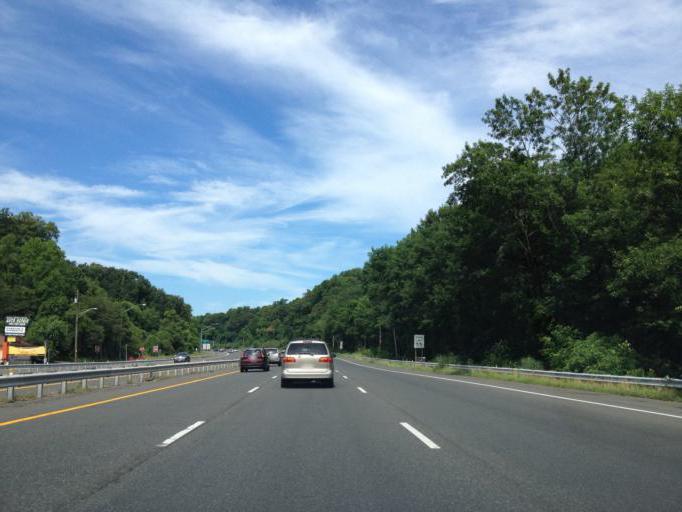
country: US
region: Maryland
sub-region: Anne Arundel County
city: Cape Saint Claire
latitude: 39.0279
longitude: -76.4561
